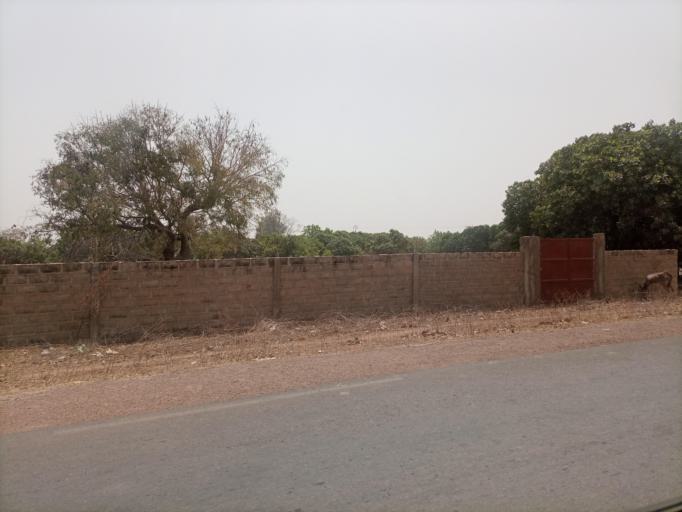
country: SN
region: Fatick
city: Sokone
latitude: 13.7171
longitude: -16.4252
